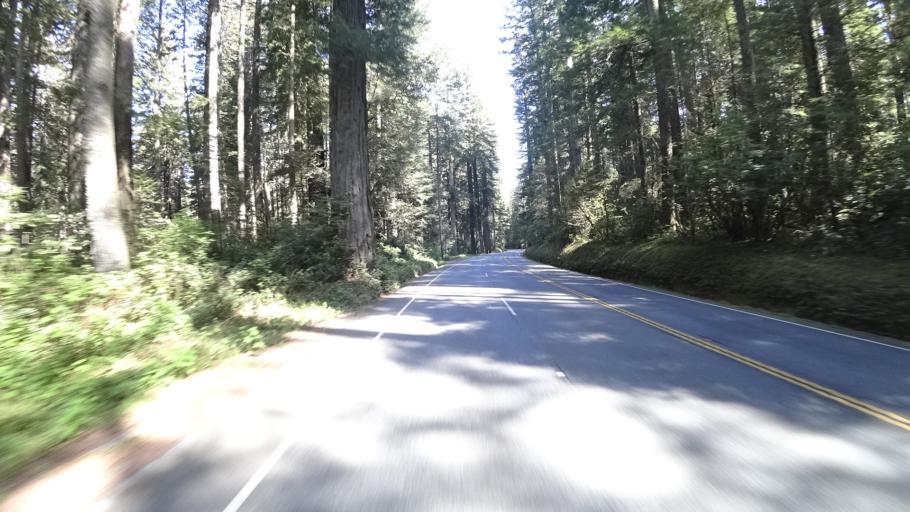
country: US
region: California
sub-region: Del Norte County
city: Bertsch-Oceanview
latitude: 41.6738
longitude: -124.1138
